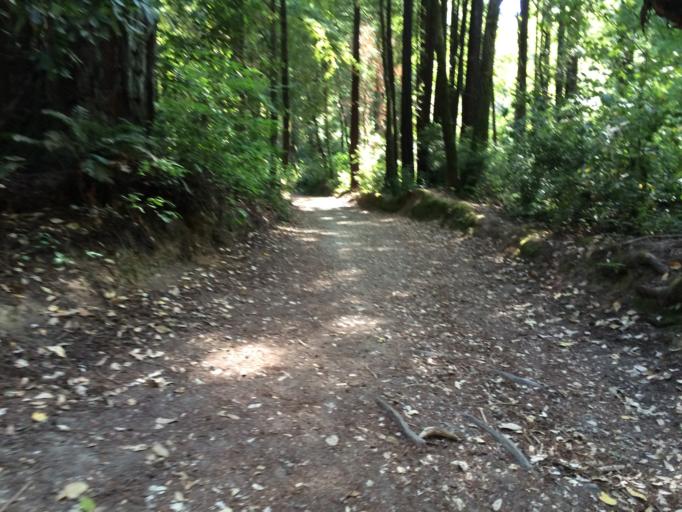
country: US
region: California
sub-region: Santa Cruz County
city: Mount Hermon
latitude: 37.0318
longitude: -122.0624
